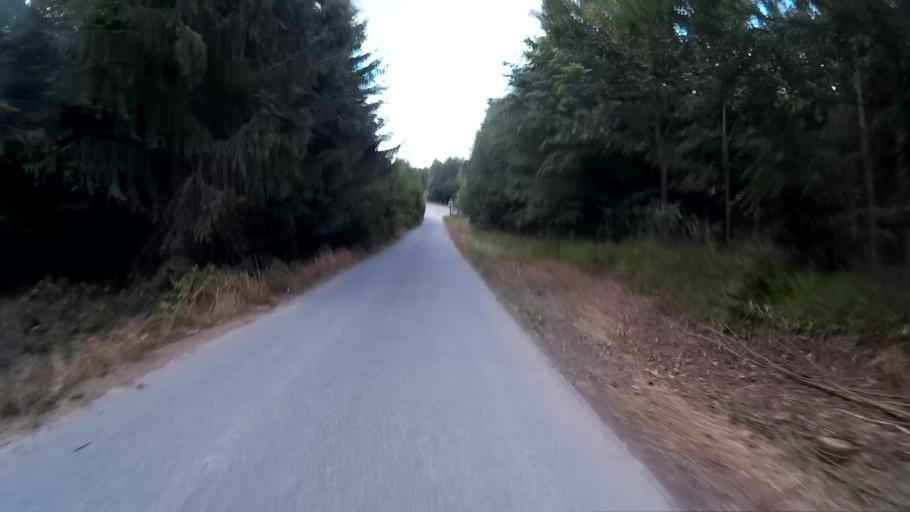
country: CZ
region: South Moravian
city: Veverska Bityska
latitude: 49.2337
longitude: 16.4663
